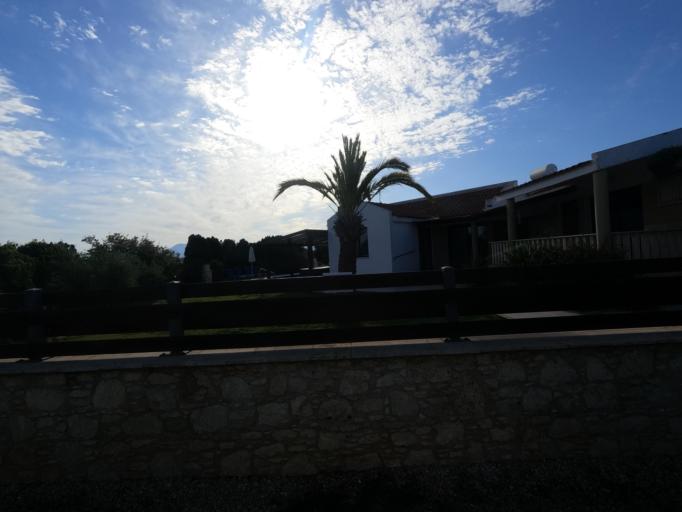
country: CY
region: Pafos
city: Polis
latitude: 35.0377
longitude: 32.3840
